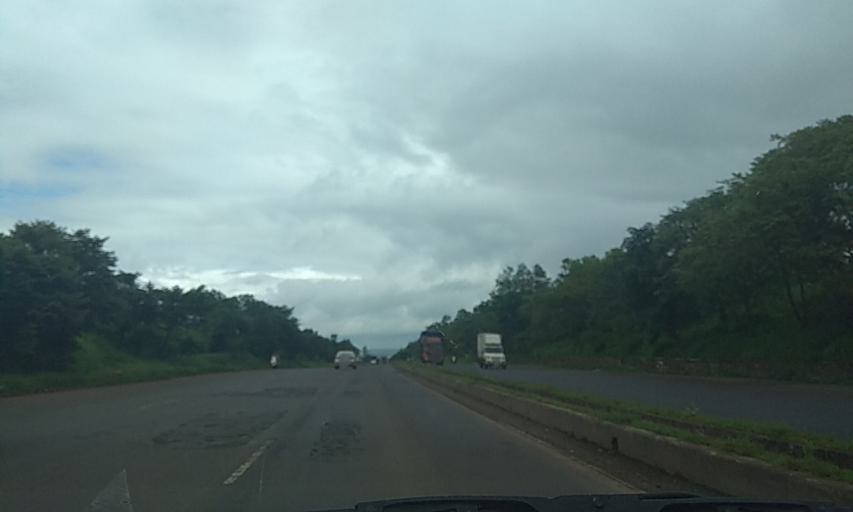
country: IN
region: Karnataka
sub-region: Belgaum
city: Belgaum
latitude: 15.8870
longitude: 74.5243
